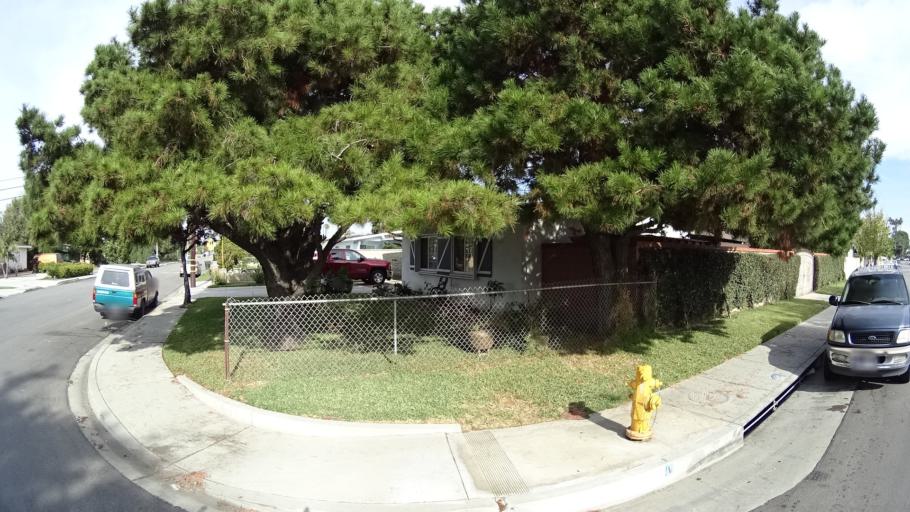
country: US
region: California
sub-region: Orange County
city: Garden Grove
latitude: 33.7839
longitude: -117.9089
